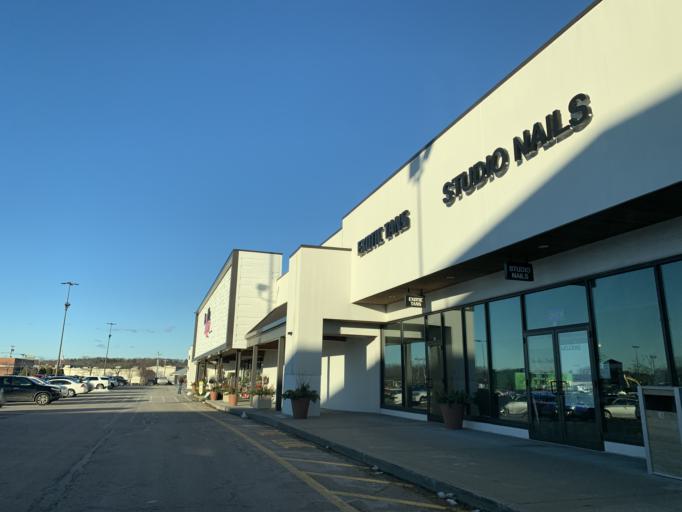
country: US
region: Rhode Island
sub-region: Kent County
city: East Greenwich
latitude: 41.6609
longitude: -71.4952
